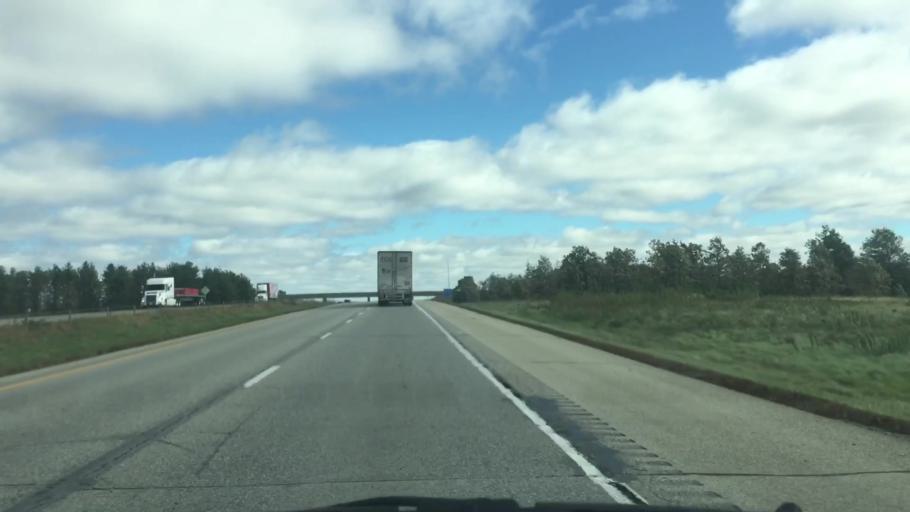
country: US
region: Iowa
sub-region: Poweshiek County
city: Grinnell
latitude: 41.6952
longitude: -92.8003
